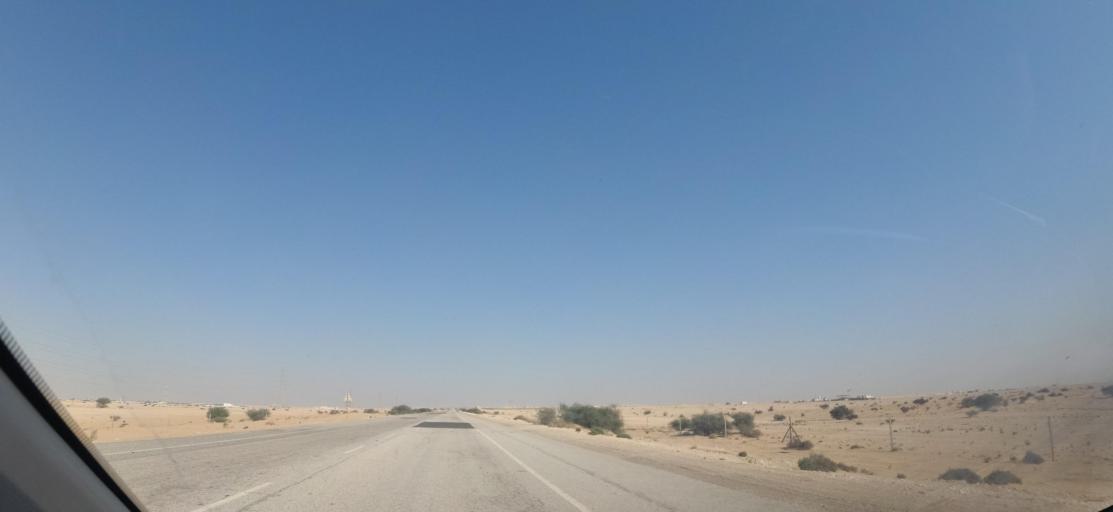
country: QA
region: Baladiyat ar Rayyan
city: Dukhan
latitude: 25.4788
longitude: 50.9539
